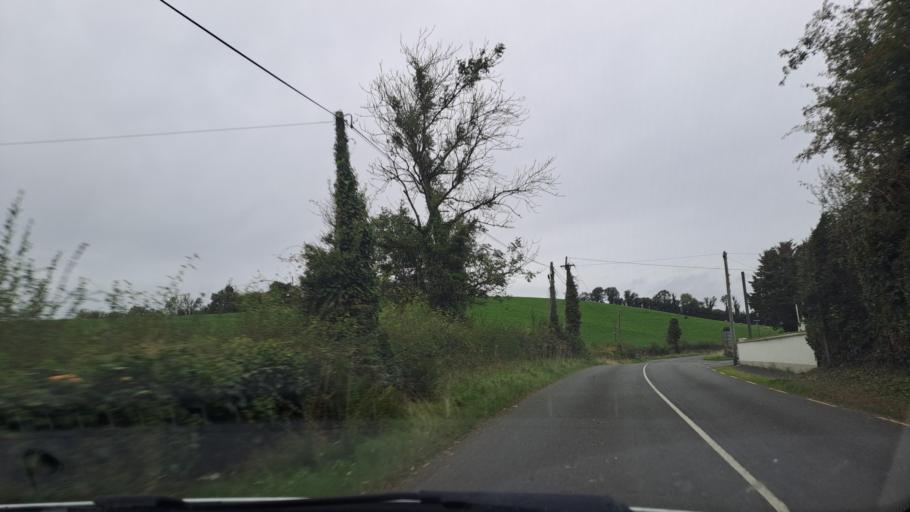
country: IE
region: Ulster
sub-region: County Monaghan
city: Carrickmacross
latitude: 53.9459
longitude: -6.6715
